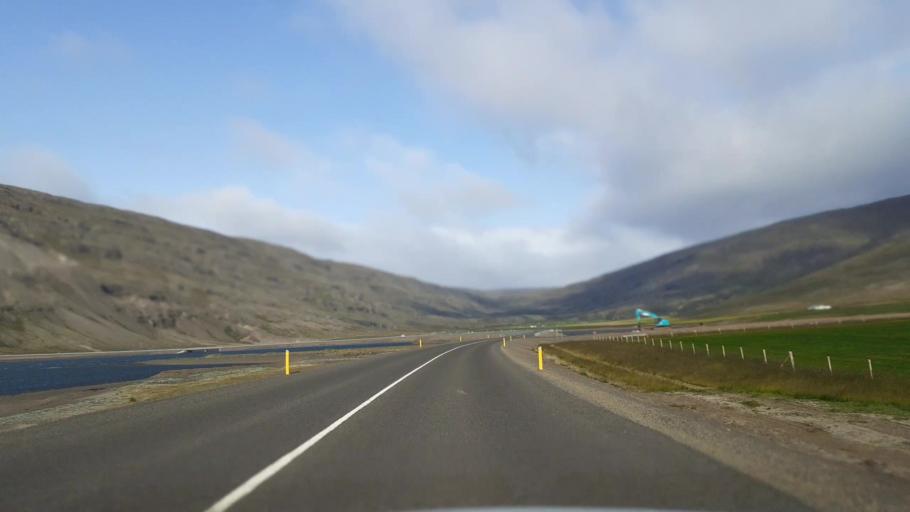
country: IS
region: East
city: Reydarfjoerdur
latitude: 64.7889
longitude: -14.4700
